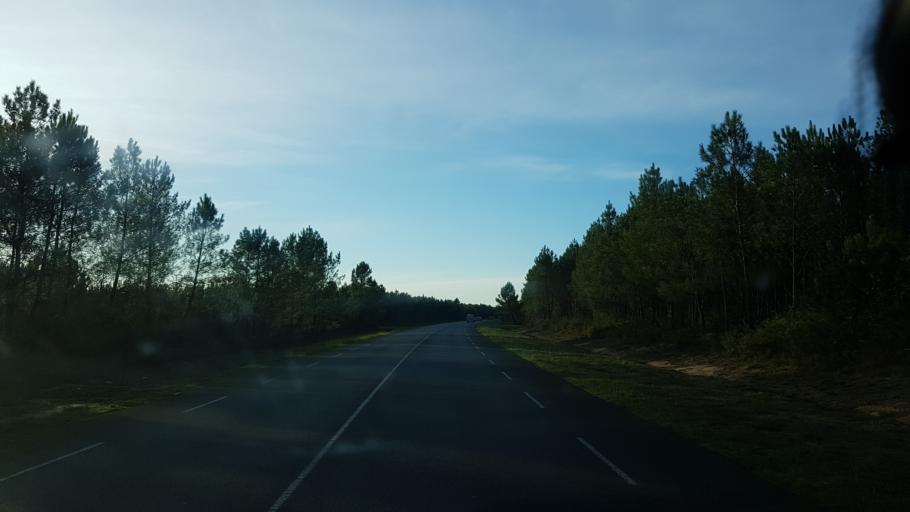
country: FR
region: Aquitaine
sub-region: Departement de la Gironde
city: Martignas-sur-Jalle
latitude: 44.8310
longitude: -0.7919
